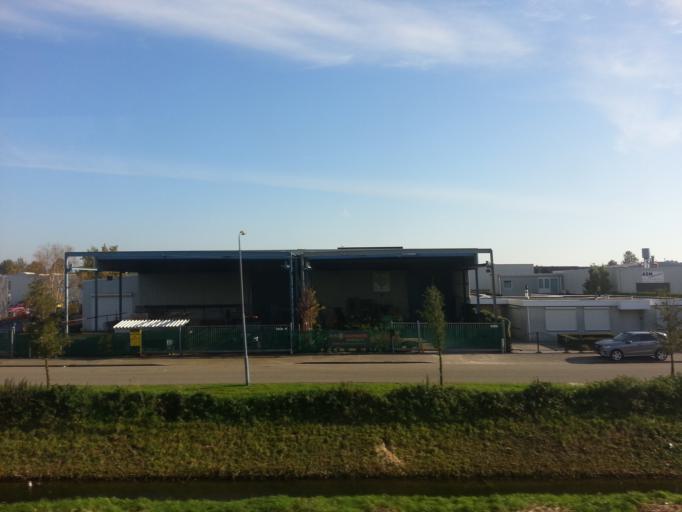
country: NL
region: North Brabant
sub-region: Gemeente 's-Hertogenbosch
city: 's-Hertogenbosch
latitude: 51.7242
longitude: 5.2842
